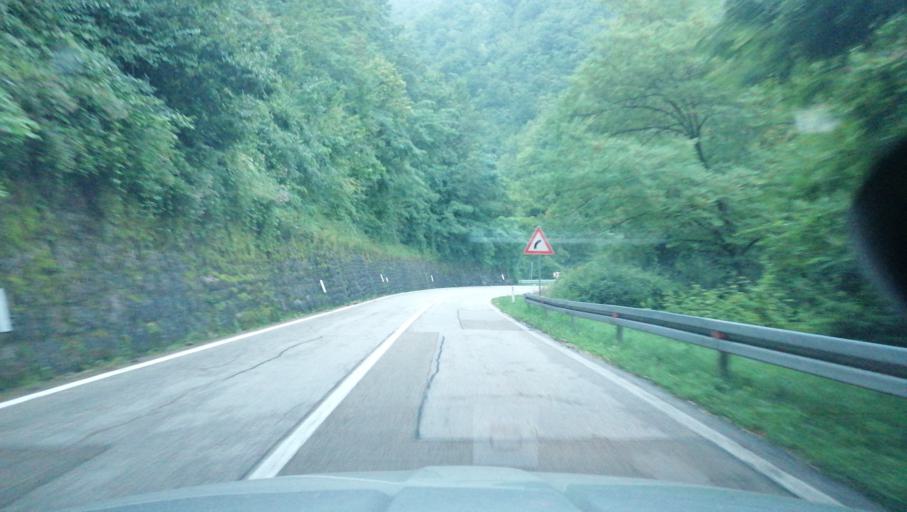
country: BA
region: Federation of Bosnia and Herzegovina
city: Jablanica
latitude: 43.7118
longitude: 17.7115
